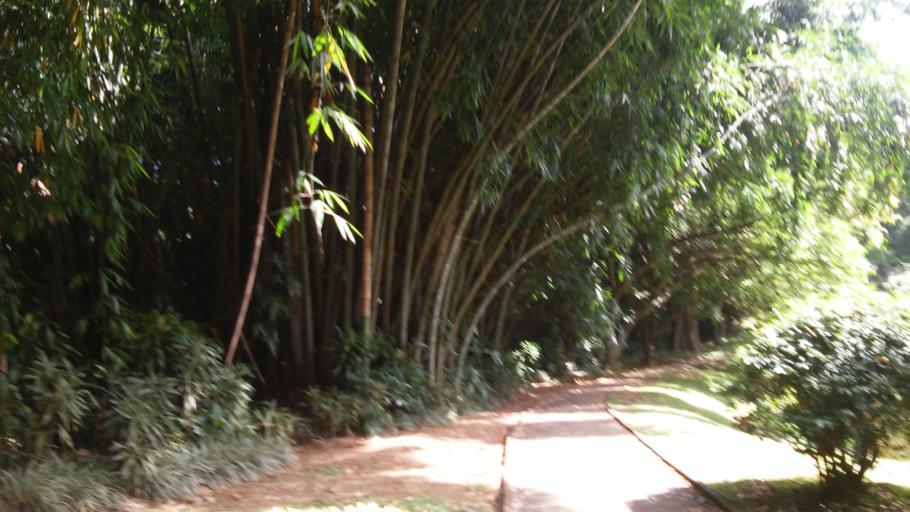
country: LK
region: Central
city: Kandy
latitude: 7.2670
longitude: 80.5941
